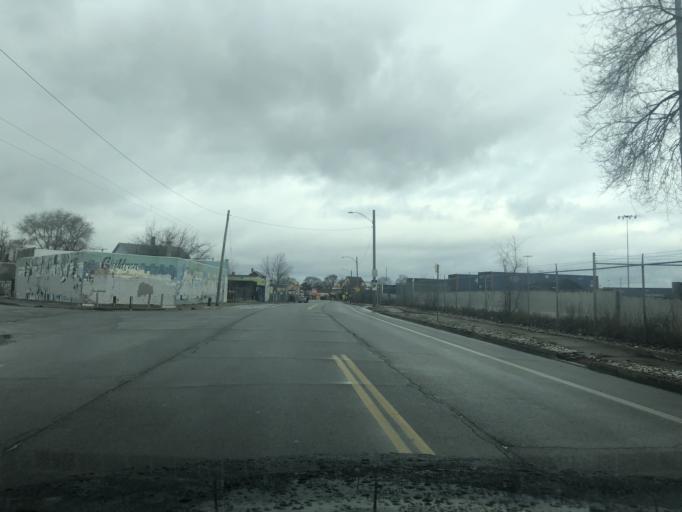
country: US
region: Michigan
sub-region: Wayne County
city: River Rouge
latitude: 42.3164
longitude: -83.1209
